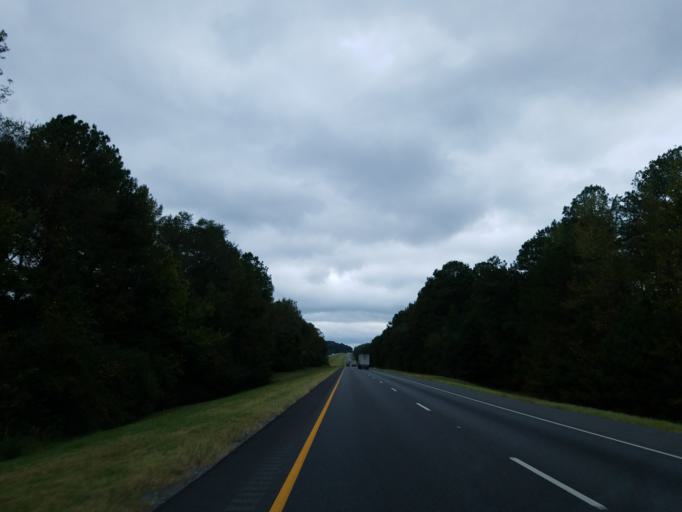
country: US
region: Alabama
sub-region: Hale County
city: Moundville
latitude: 33.0031
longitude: -87.7676
